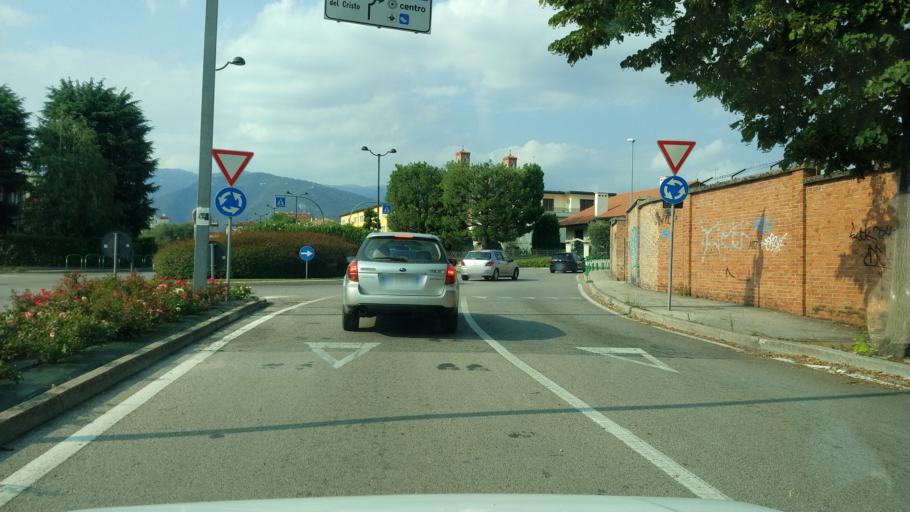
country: IT
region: Veneto
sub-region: Provincia di Vicenza
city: Bassano del Grappa
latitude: 45.7601
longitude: 11.7317
